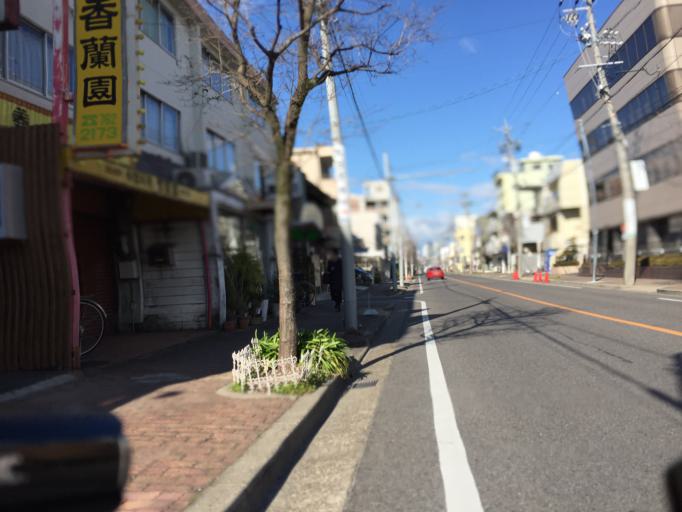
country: JP
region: Aichi
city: Nagoya-shi
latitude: 35.1616
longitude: 136.9435
